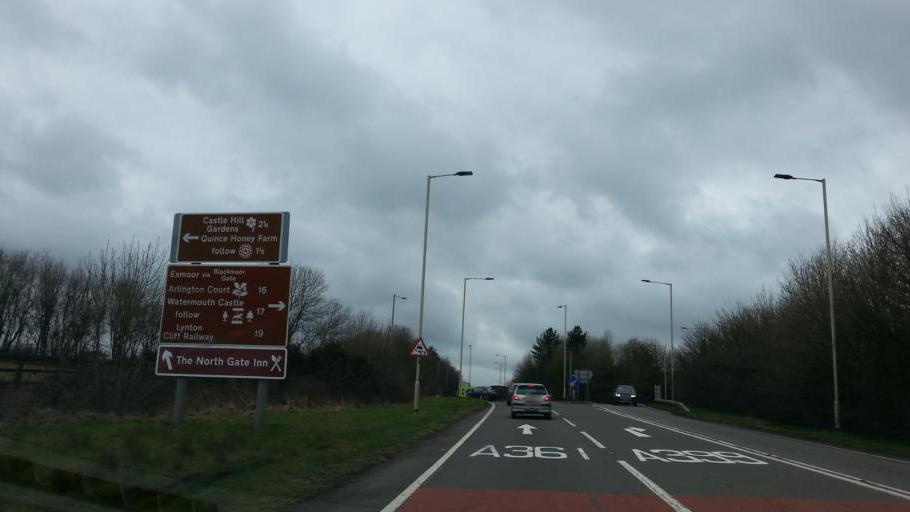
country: GB
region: England
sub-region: Devon
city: South Molton
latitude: 51.0380
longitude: -3.8545
